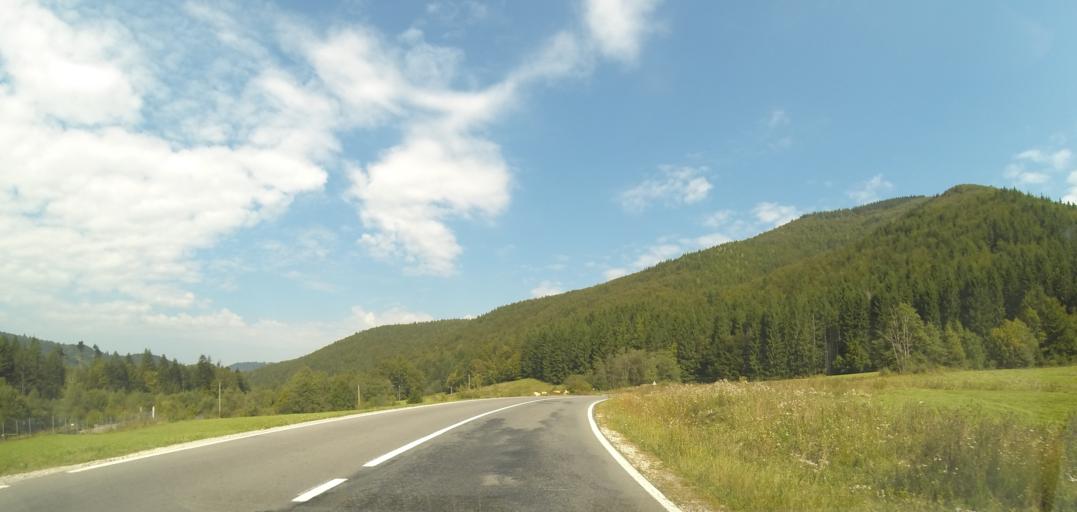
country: RO
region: Brasov
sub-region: Comuna Tarlungeni
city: Zizin
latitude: 45.5387
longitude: 25.8346
